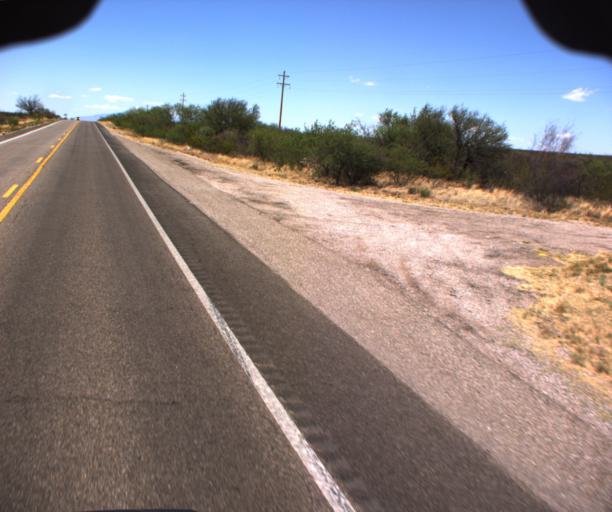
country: US
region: Arizona
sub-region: Cochise County
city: Tombstone
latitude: 31.7658
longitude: -110.1184
